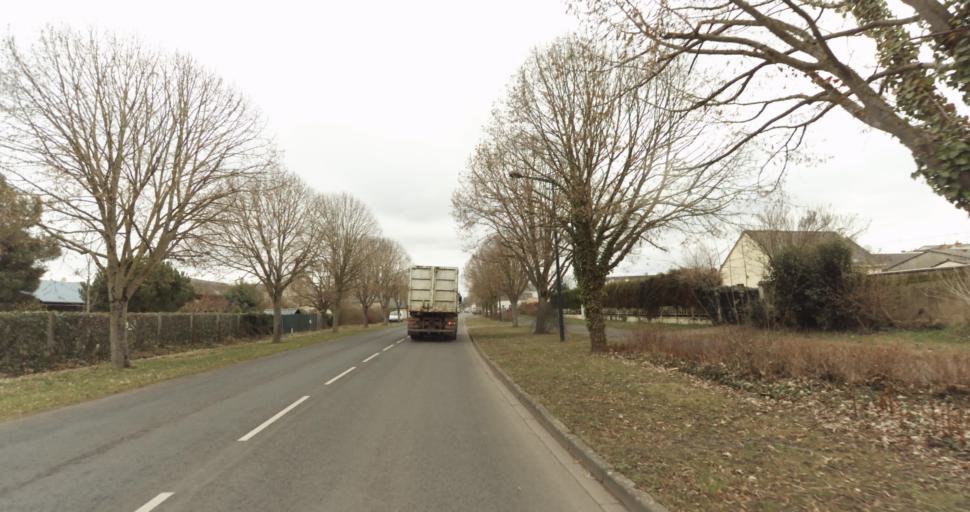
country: FR
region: Pays de la Loire
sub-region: Departement de Maine-et-Loire
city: Saumur
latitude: 47.2729
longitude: -0.0664
